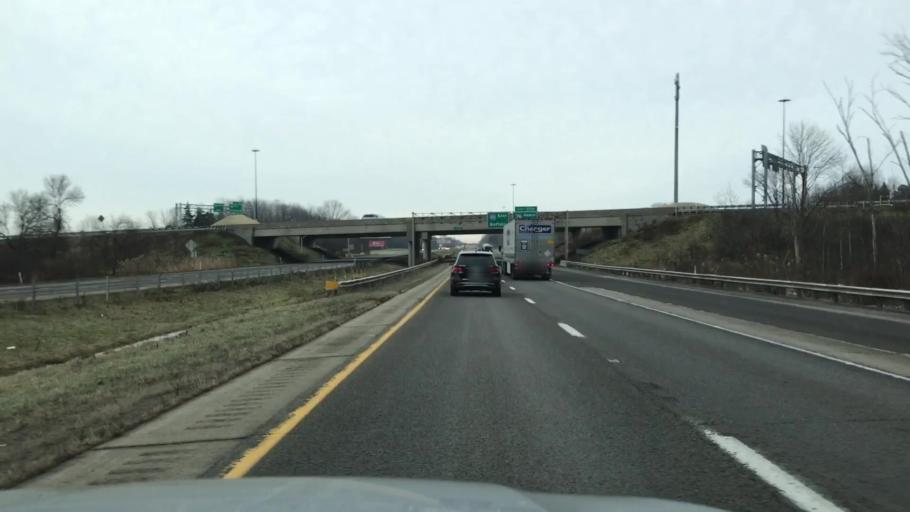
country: US
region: Pennsylvania
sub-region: Erie County
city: Erie
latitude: 42.0308
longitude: -80.1244
